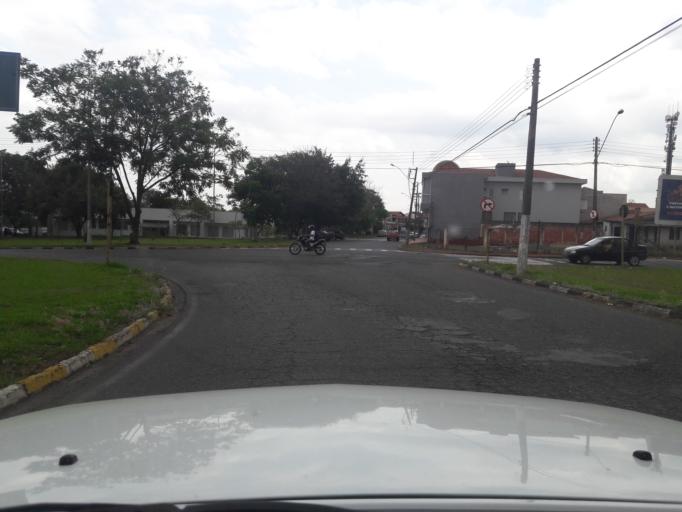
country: BR
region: Sao Paulo
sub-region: Moji-Guacu
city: Mogi-Gaucu
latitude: -22.3465
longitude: -46.9398
